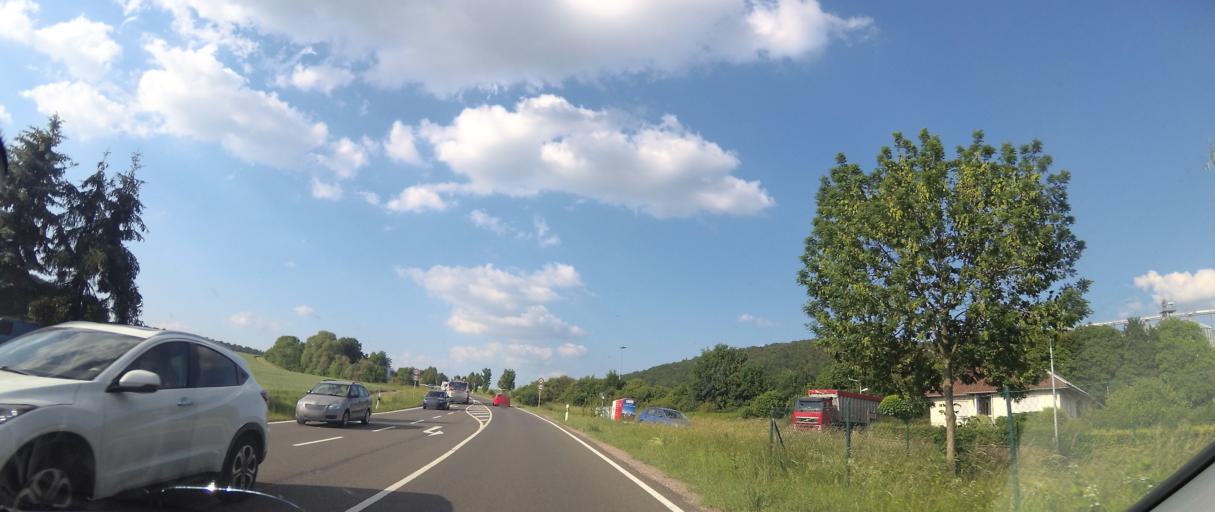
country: DE
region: Rheinland-Pfalz
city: Furfeld
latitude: 49.7807
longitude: 7.8894
